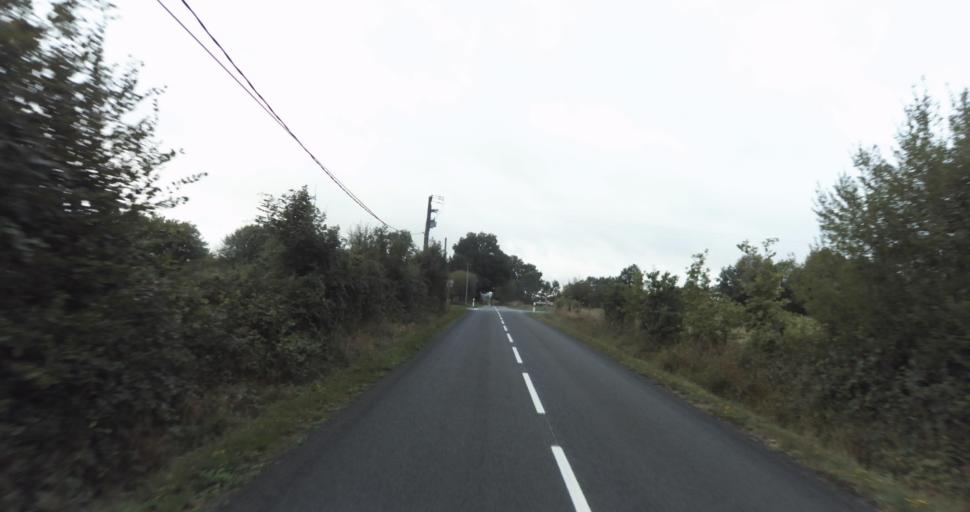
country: FR
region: Lower Normandy
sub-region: Departement de l'Orne
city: Sainte-Gauburge-Sainte-Colombe
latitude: 48.7462
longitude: 0.4377
